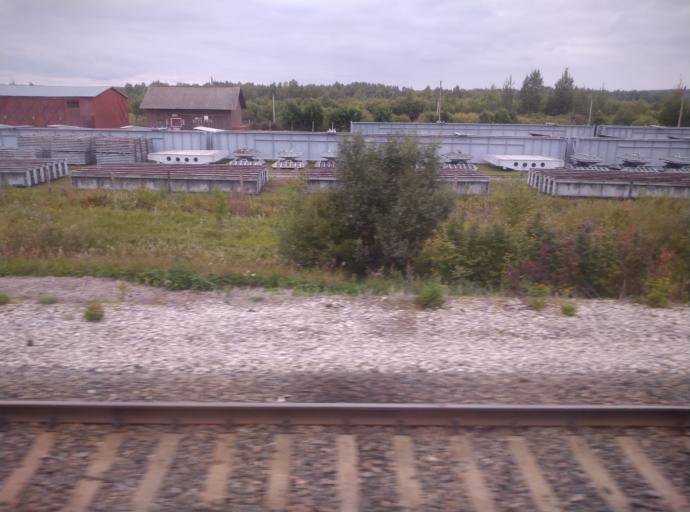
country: RU
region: Kostroma
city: Kosmynino
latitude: 57.5913
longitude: 40.7667
